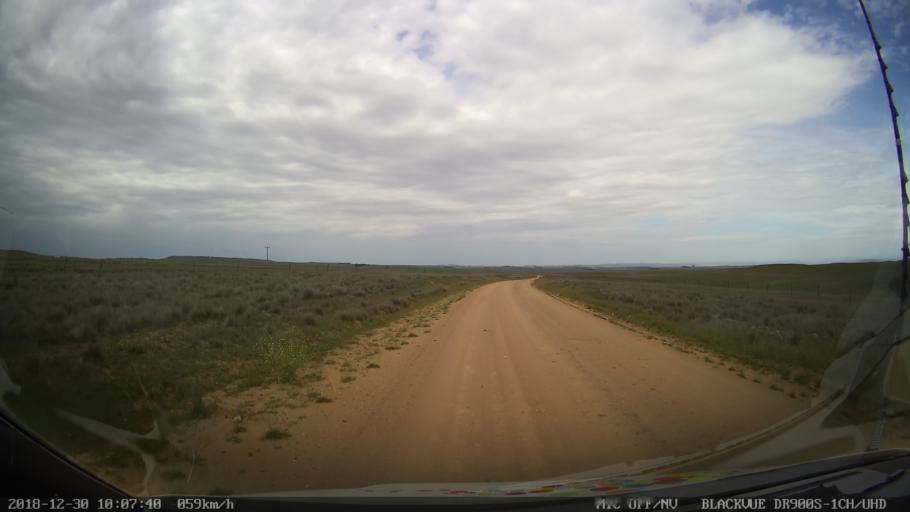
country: AU
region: New South Wales
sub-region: Cooma-Monaro
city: Cooma
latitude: -36.5408
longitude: 149.1210
